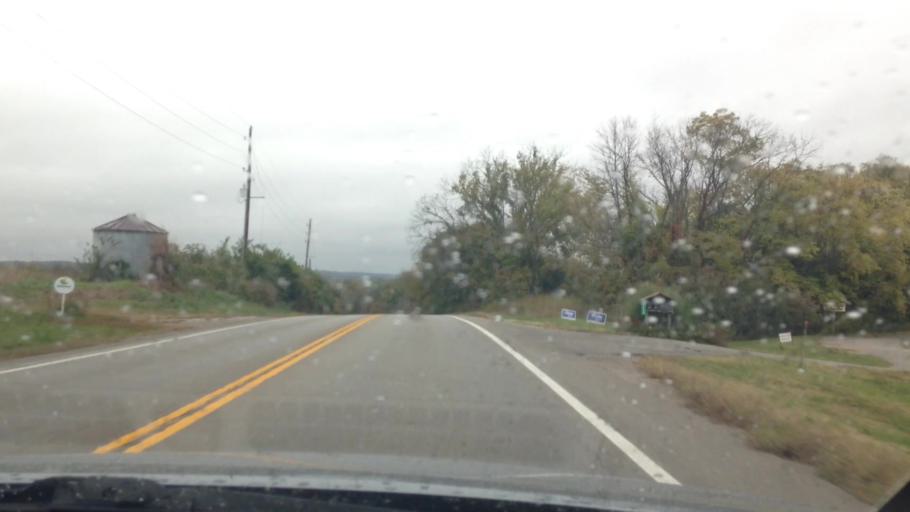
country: US
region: Missouri
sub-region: Platte County
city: Weston
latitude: 39.4074
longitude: -94.8678
